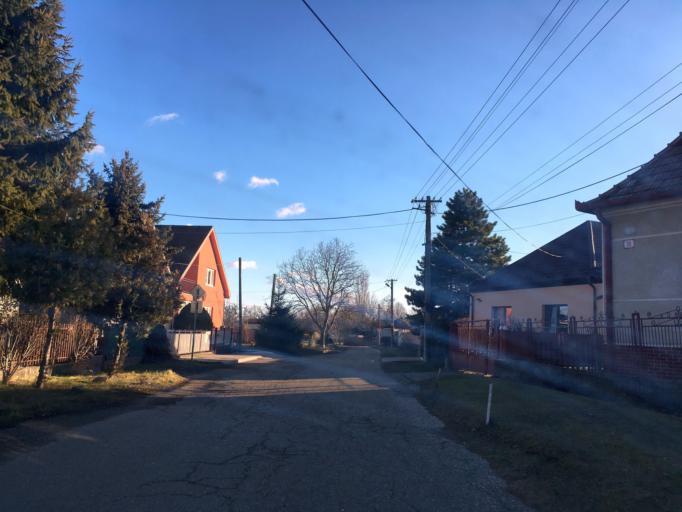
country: SK
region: Trnavsky
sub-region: Okres Dunajska Streda
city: Velky Meder
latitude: 47.8858
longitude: 17.8122
